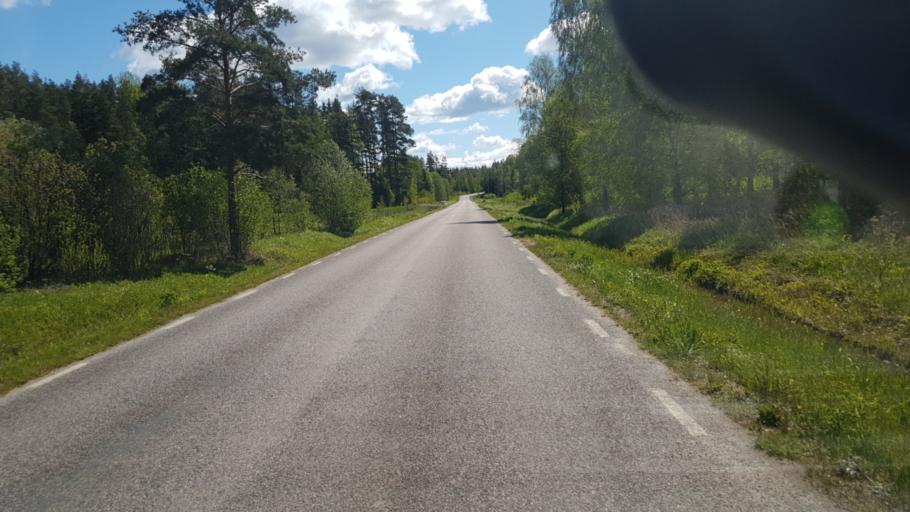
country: SE
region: Vaermland
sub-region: Arvika Kommun
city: Arvika
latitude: 59.5188
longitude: 12.8396
